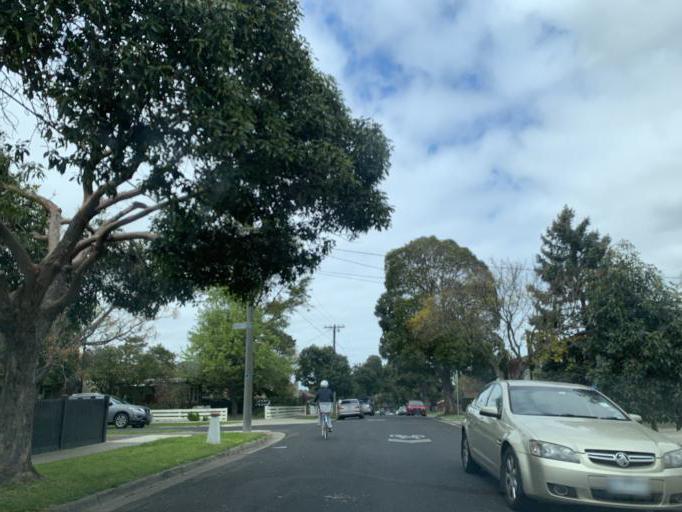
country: AU
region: Victoria
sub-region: Moreland
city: Pascoe Vale
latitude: -37.7241
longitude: 144.9369
